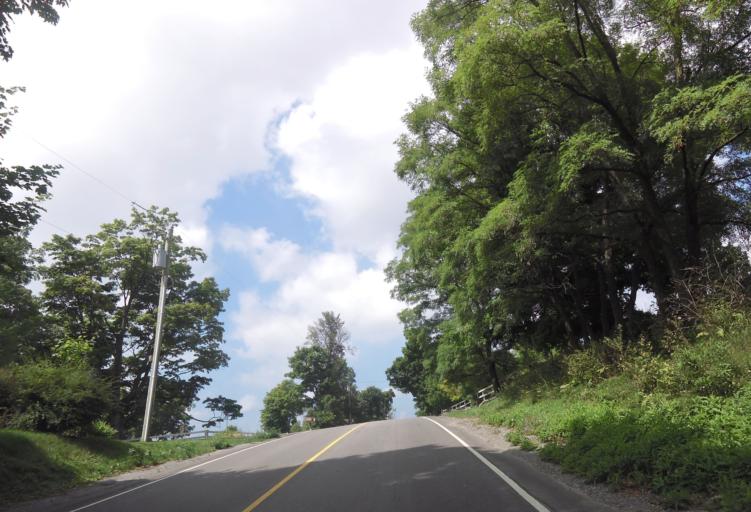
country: CA
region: Ontario
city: Oshawa
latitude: 43.9868
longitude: -78.8702
